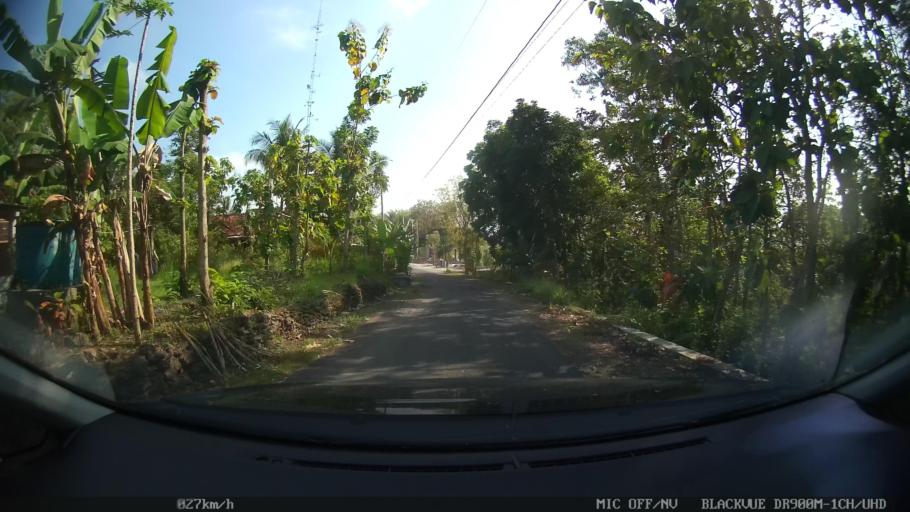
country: ID
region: Daerah Istimewa Yogyakarta
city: Kasihan
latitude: -7.8320
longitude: 110.2876
